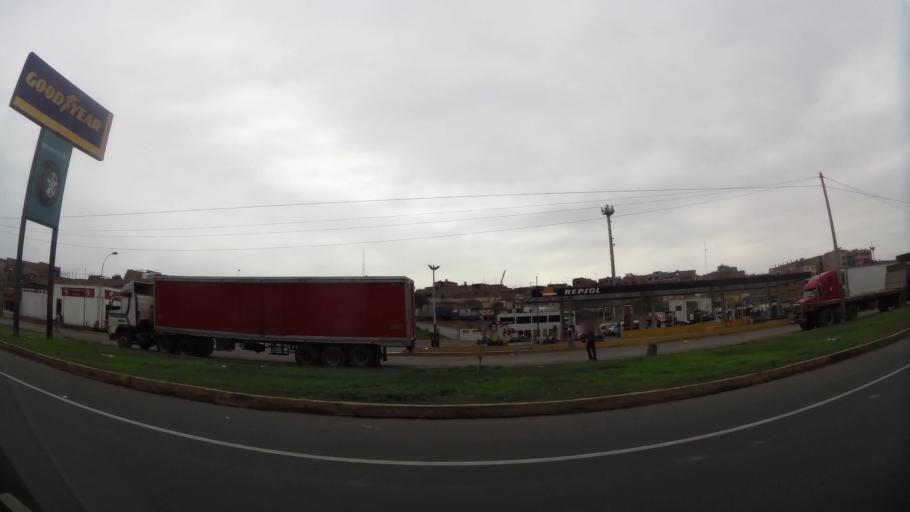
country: PE
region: Lima
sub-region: Lima
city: Surco
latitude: -12.2002
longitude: -76.9739
